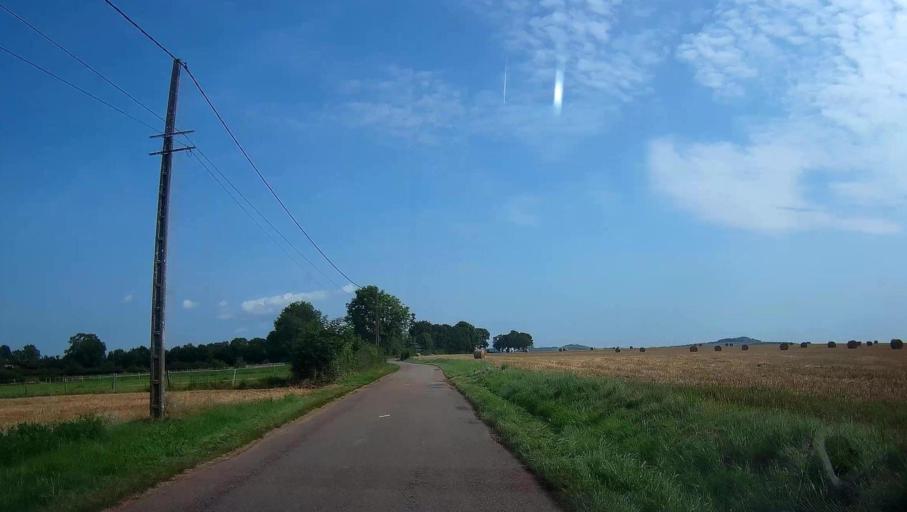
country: FR
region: Bourgogne
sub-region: Departement de Saone-et-Loire
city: Saint-Leger-sur-Dheune
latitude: 46.8956
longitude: 4.6226
